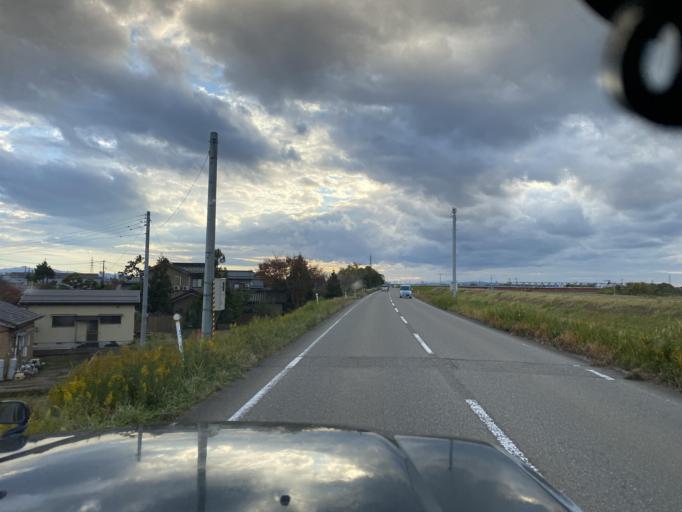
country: JP
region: Niigata
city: Sanjo
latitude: 37.6487
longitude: 138.9552
